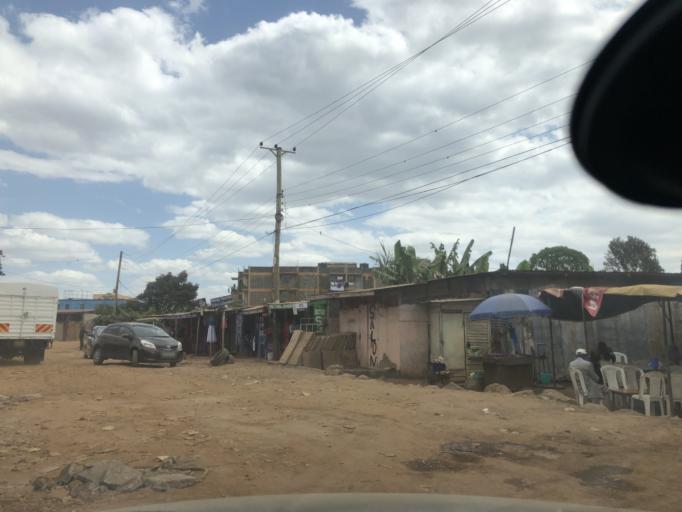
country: KE
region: Nairobi Area
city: Pumwani
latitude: -1.2301
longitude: 36.8771
